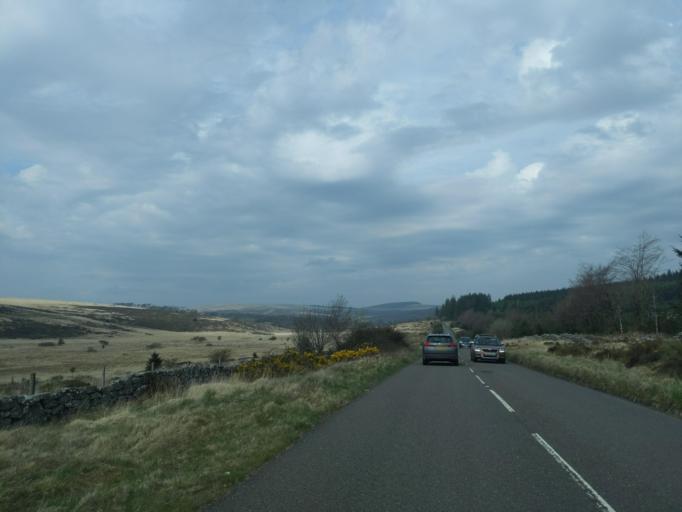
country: GB
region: England
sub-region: Devon
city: Okehampton
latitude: 50.5806
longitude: -3.9277
